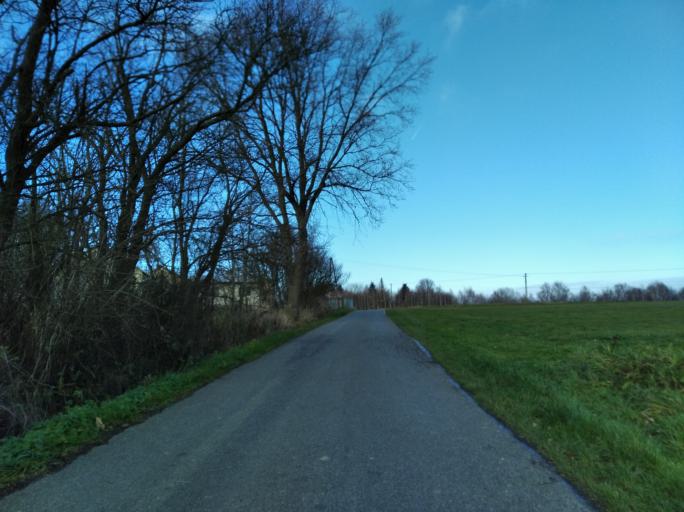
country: PL
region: Subcarpathian Voivodeship
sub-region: Powiat strzyzowski
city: Czudec
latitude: 49.9134
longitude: 21.8466
